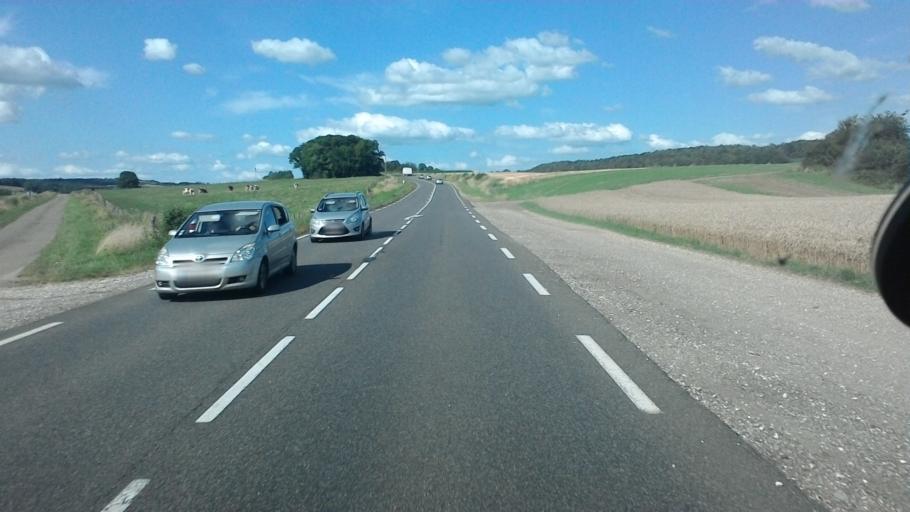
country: FR
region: Franche-Comte
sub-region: Departement de la Haute-Saone
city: Echenoz-la-Meline
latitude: 47.5491
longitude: 6.0603
